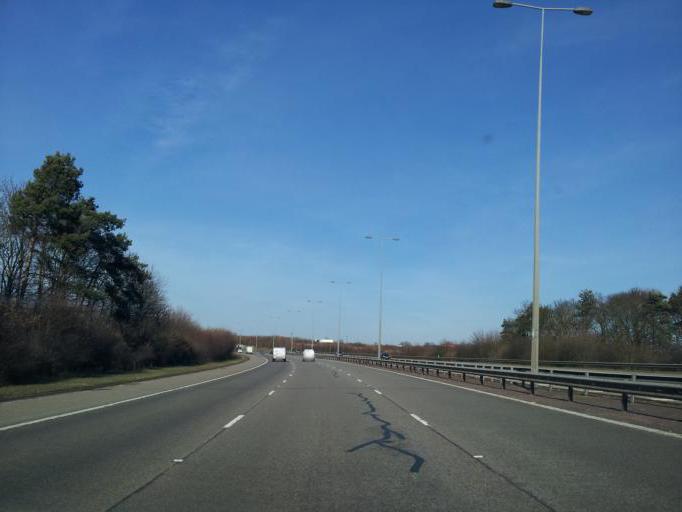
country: GB
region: England
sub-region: Cambridgeshire
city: Great Stukeley
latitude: 52.3715
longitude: -0.2529
